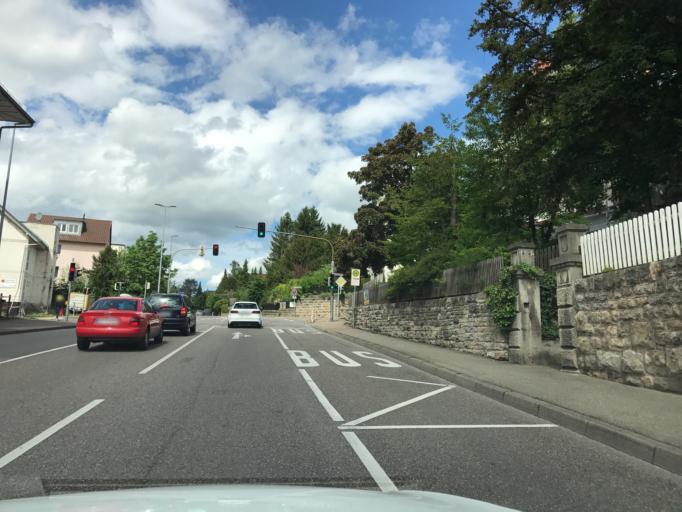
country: DE
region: Baden-Wuerttemberg
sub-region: Regierungsbezirk Stuttgart
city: Bietigheim-Bissingen
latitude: 48.9619
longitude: 9.1243
